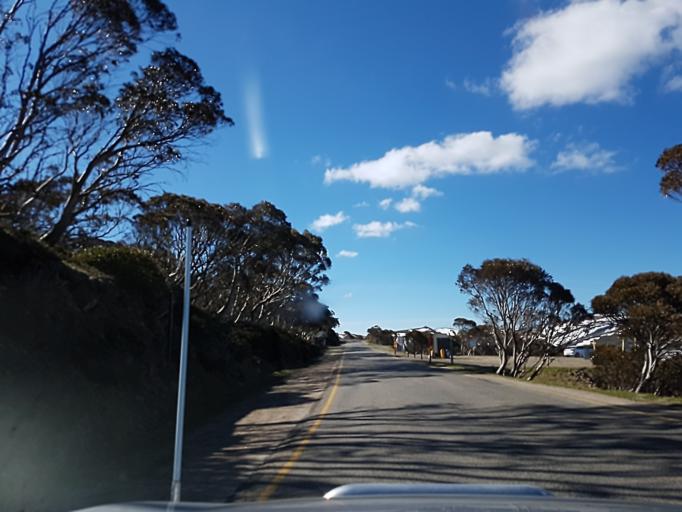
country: AU
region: Victoria
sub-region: Alpine
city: Mount Beauty
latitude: -36.9894
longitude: 147.1486
